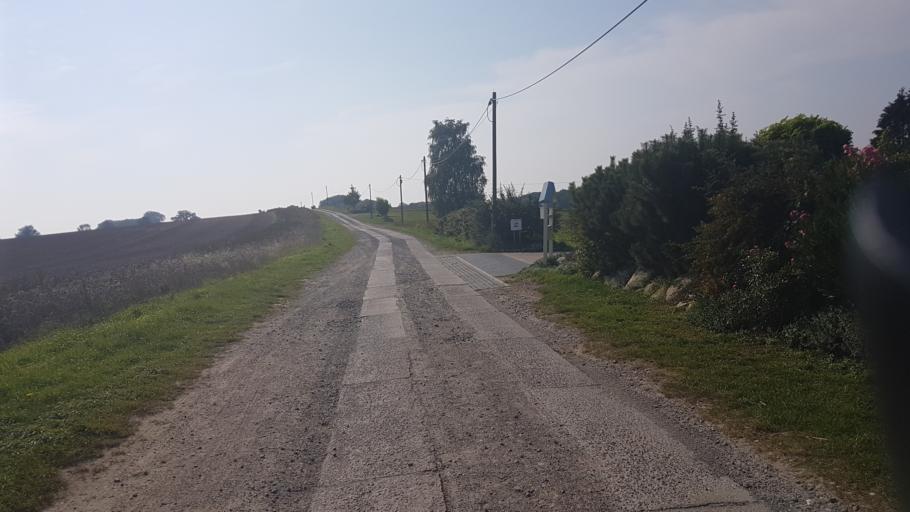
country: DE
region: Mecklenburg-Vorpommern
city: Putbus
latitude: 54.3261
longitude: 13.4581
